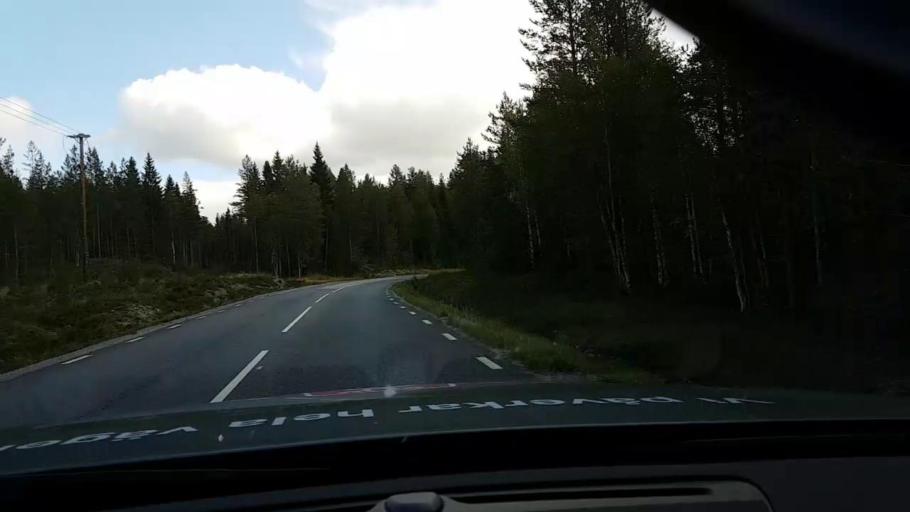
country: SE
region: Vaesterbotten
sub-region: Asele Kommun
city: Asele
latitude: 63.8076
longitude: 17.5383
